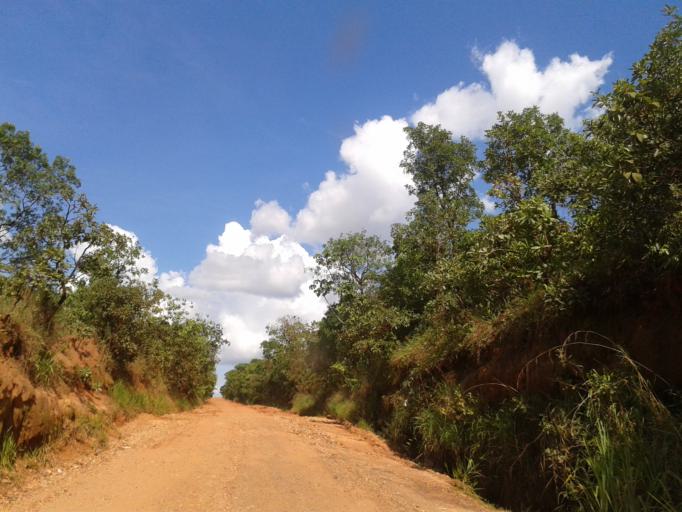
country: BR
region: Minas Gerais
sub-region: Campina Verde
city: Campina Verde
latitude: -19.3272
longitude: -49.7910
